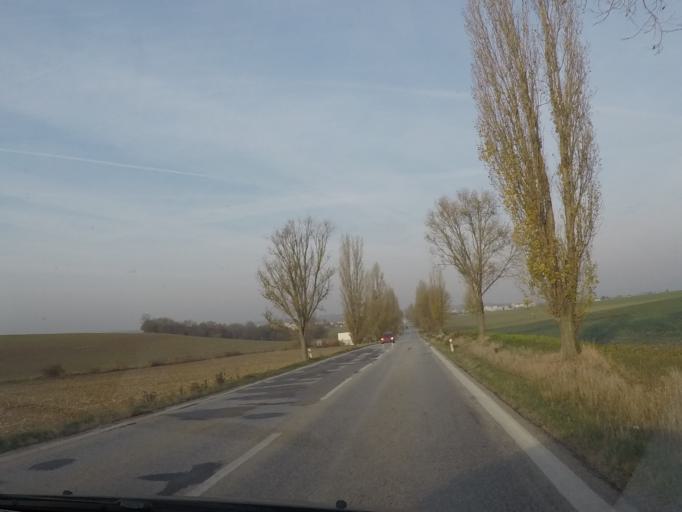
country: SK
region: Nitriansky
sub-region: Okres Nitra
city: Vrable
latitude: 48.2369
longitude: 18.3341
